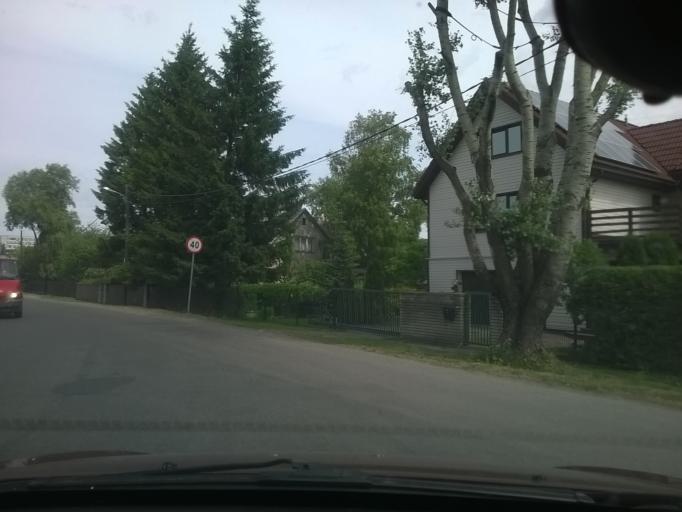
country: EE
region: Harju
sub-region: Tallinna linn
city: Tallinn
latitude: 59.4257
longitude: 24.6899
